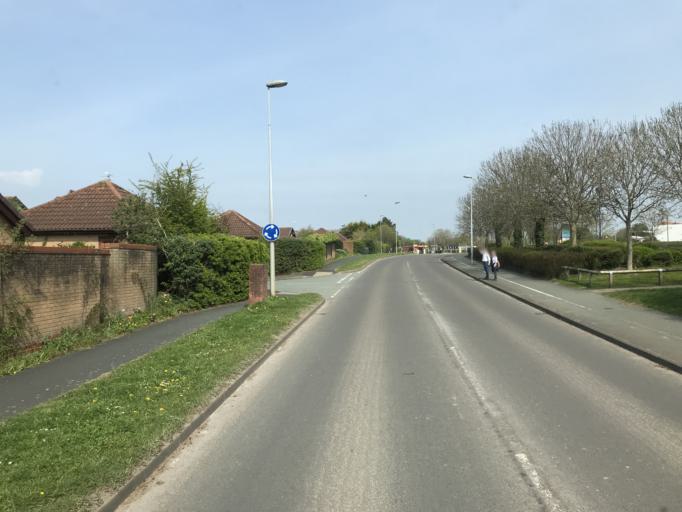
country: GB
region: England
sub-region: Cheshire West and Chester
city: Hoole
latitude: 53.1823
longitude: -2.8584
